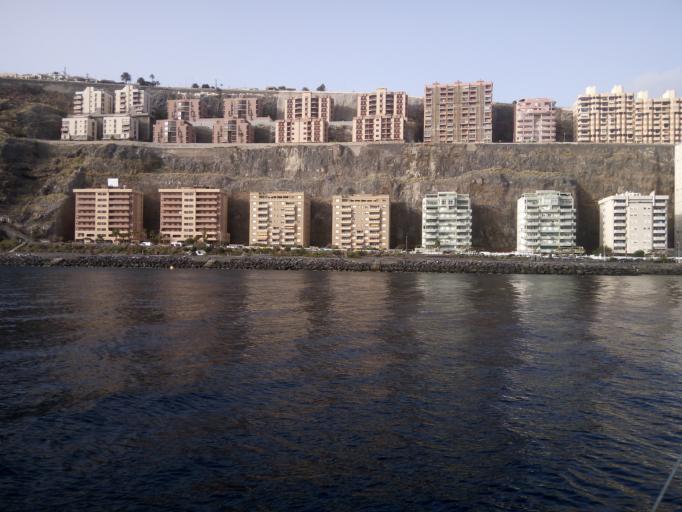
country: ES
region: Canary Islands
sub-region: Provincia de Santa Cruz de Tenerife
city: Candelaria
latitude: 28.3999
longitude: -16.3256
